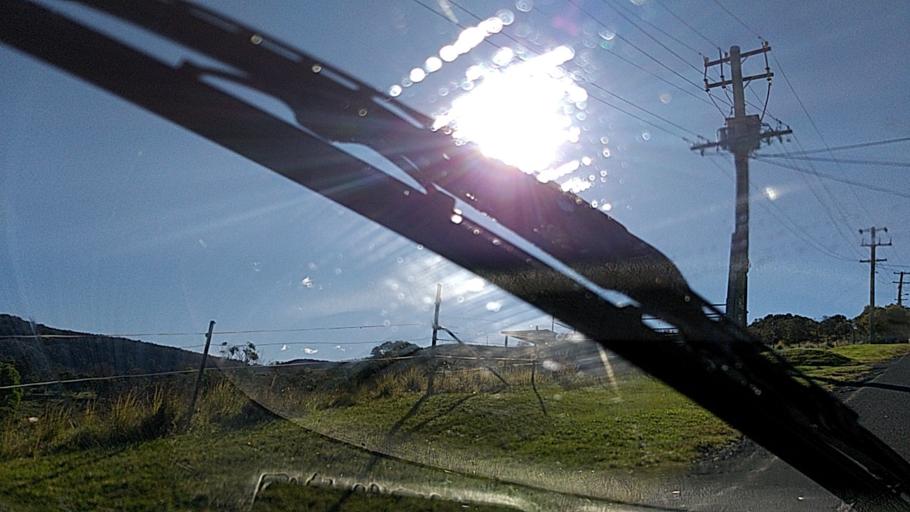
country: AU
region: New South Wales
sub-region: Wollongong
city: Cordeaux Heights
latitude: -34.4282
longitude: 150.8428
